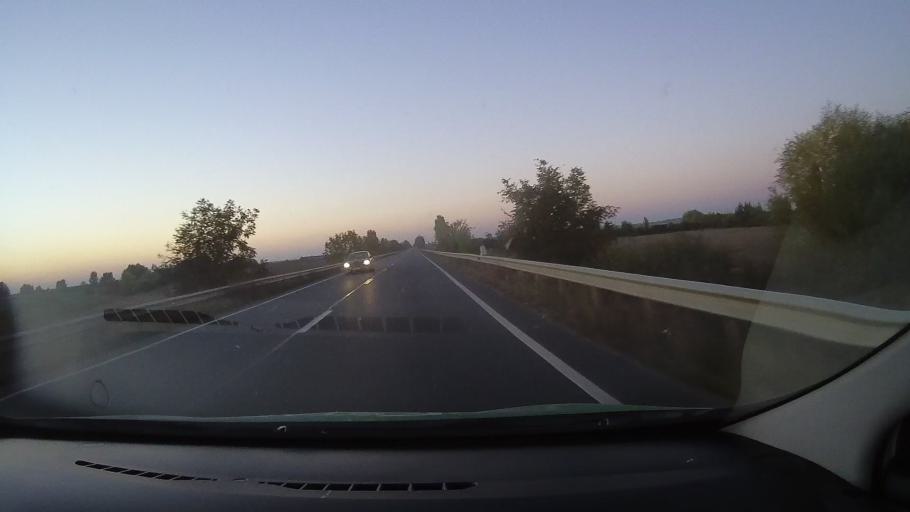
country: RO
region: Bihor
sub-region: Comuna Valea lui Mihai
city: Valea lui Mihai
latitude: 47.4894
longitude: 22.1563
